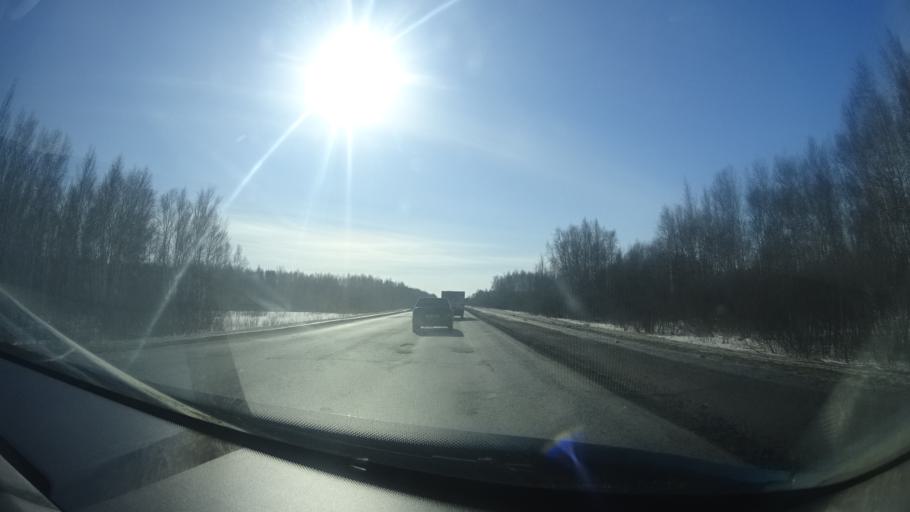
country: RU
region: Bashkortostan
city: Mikhaylovka
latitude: 54.9062
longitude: 55.7293
